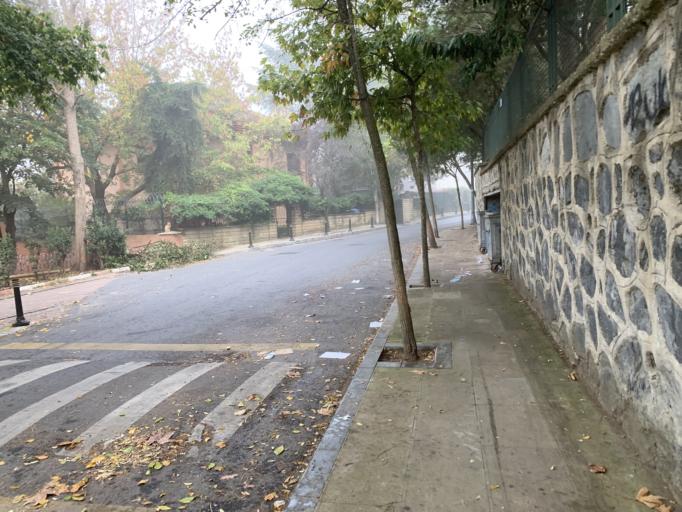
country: TR
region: Istanbul
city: Sisli
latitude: 41.0799
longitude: 29.0168
